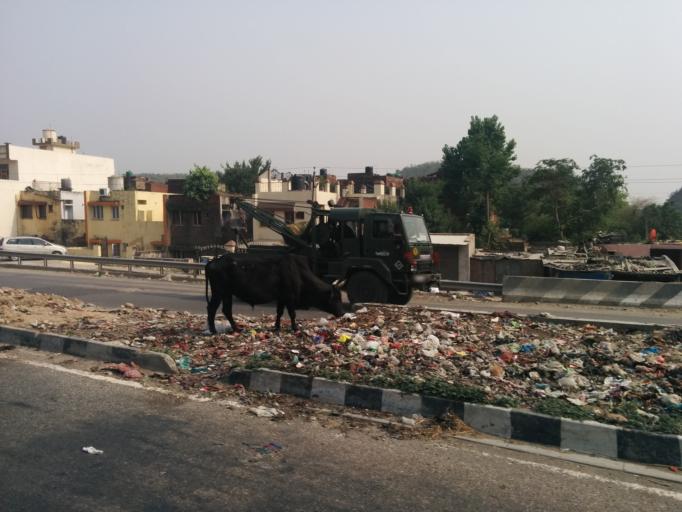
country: IN
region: Punjab
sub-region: Pathankot
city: Pathankot
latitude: 32.2541
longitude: 75.6519
